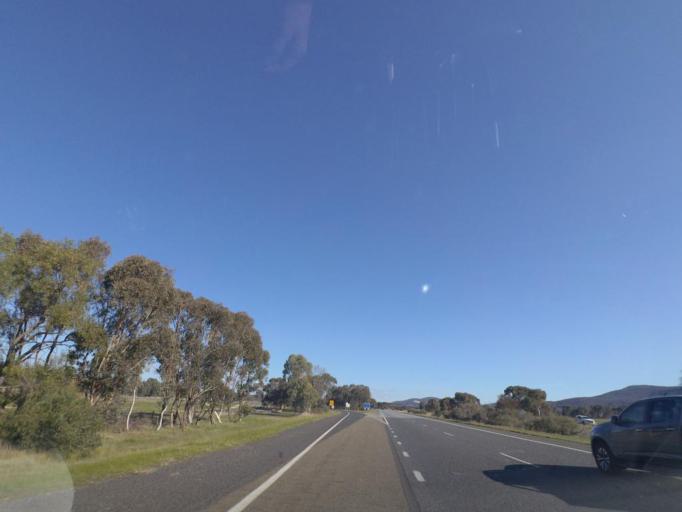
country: AU
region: Victoria
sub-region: Wangaratta
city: Wangaratta
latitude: -36.4211
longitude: 146.2642
